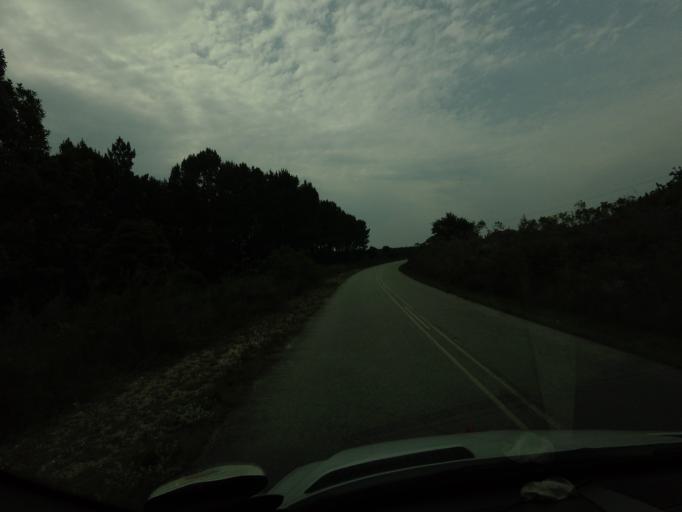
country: ZA
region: Eastern Cape
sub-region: Cacadu District Municipality
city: Kareedouw
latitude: -33.9832
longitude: 23.8422
